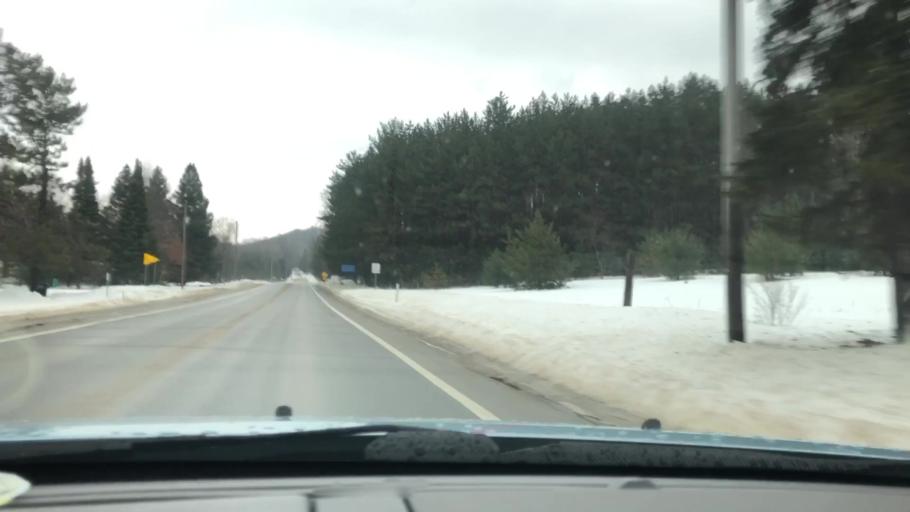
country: US
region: Michigan
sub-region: Charlevoix County
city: East Jordan
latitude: 45.1324
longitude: -85.0872
